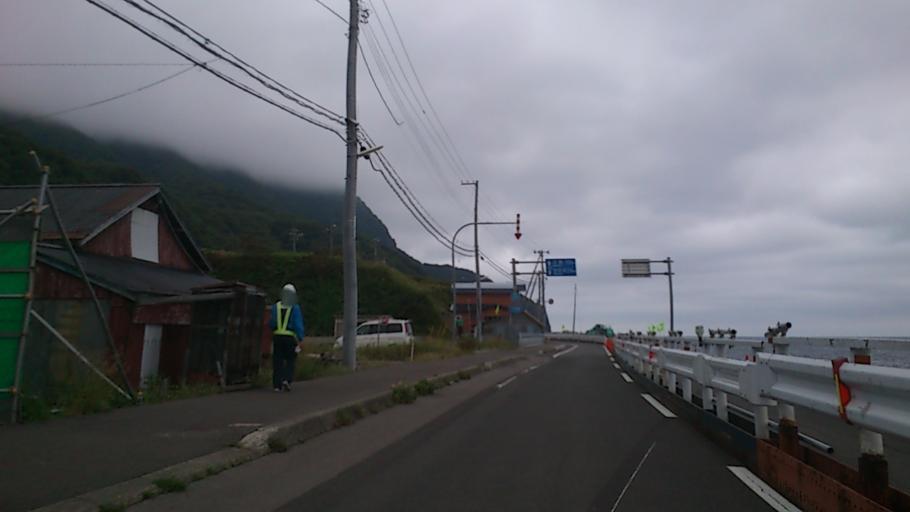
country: JP
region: Hokkaido
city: Iwanai
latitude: 42.6751
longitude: 139.8906
